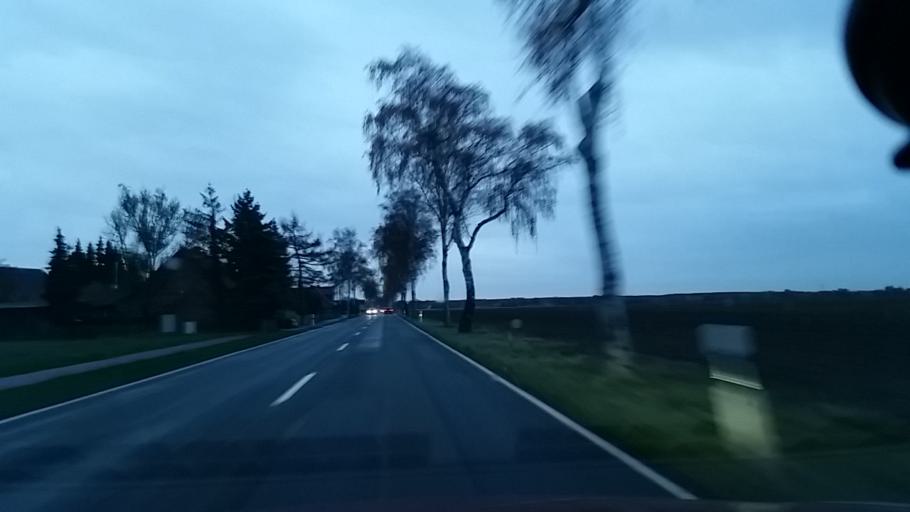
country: DE
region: Lower Saxony
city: Bodenteich
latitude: 52.8129
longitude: 10.6976
